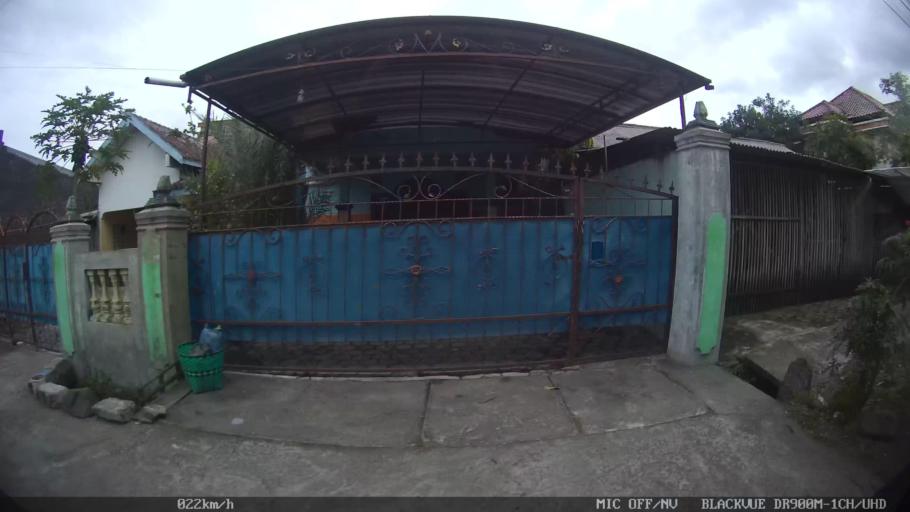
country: ID
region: Daerah Istimewa Yogyakarta
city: Depok
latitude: -7.8169
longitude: 110.4164
